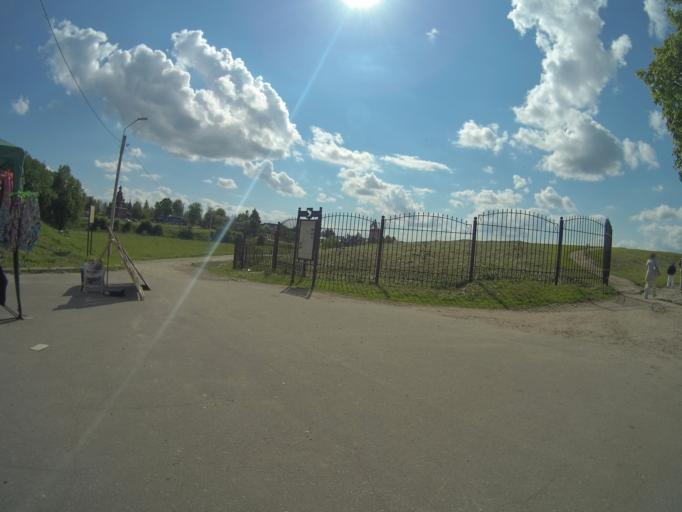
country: RU
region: Vladimir
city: Suzdal'
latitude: 56.4151
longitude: 40.4422
